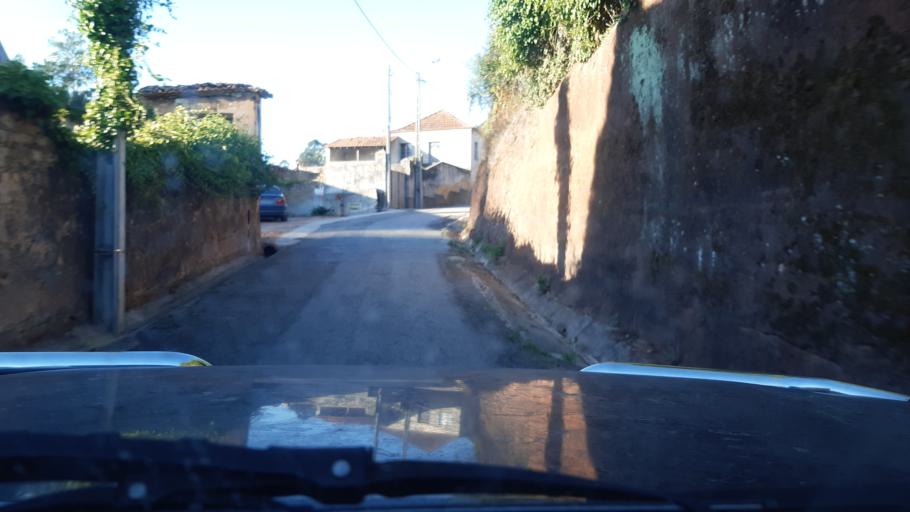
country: PT
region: Aveiro
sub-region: Agueda
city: Agueda
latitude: 40.5764
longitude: -8.4656
